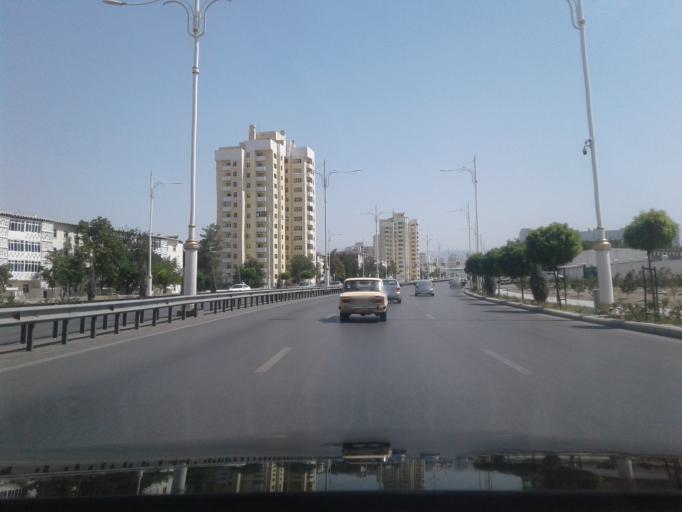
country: TM
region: Ahal
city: Ashgabat
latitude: 37.9177
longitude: 58.3894
